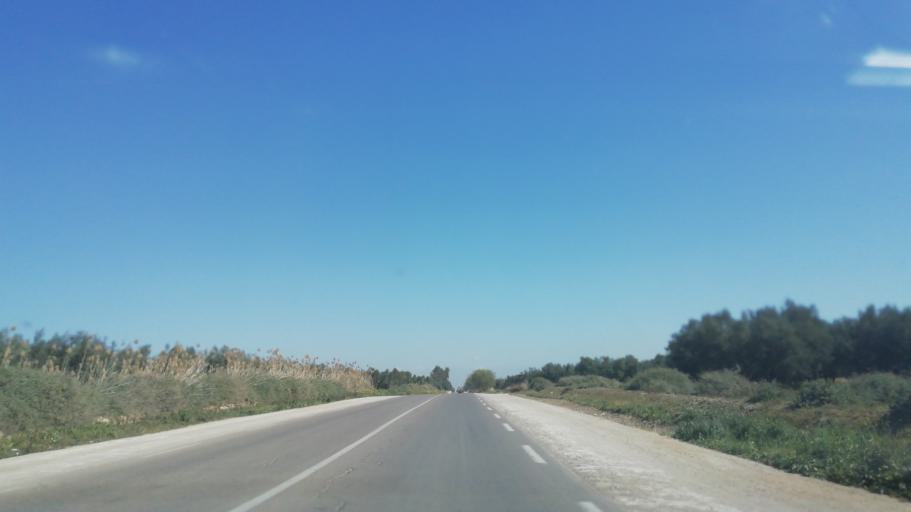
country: DZ
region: Mascara
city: Sig
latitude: 35.5390
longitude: -0.1335
